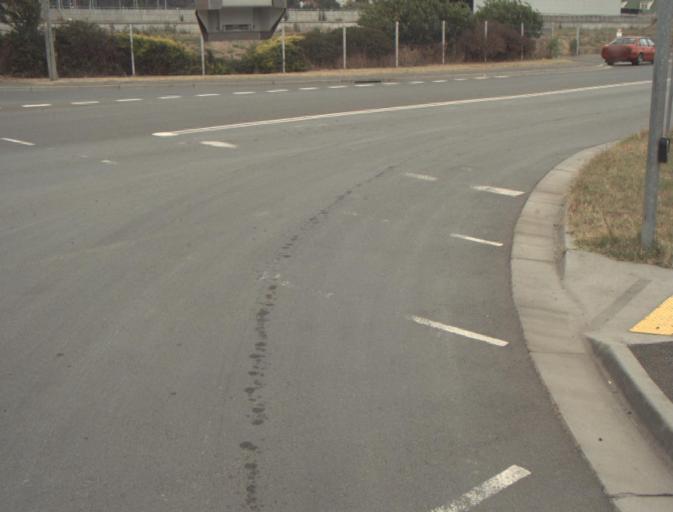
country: AU
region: Tasmania
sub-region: Launceston
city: Launceston
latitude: -41.4306
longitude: 147.1329
